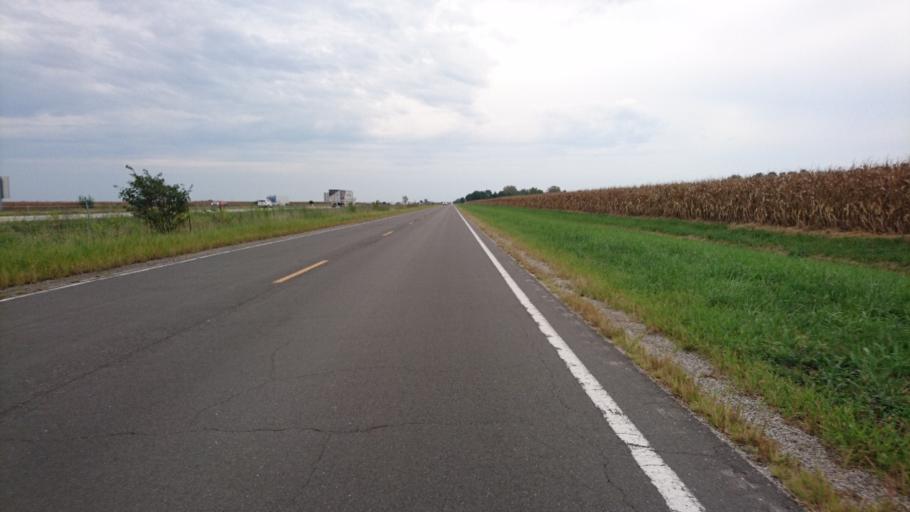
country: US
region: Illinois
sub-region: Sangamon County
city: Chatham
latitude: 39.6659
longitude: -89.6480
